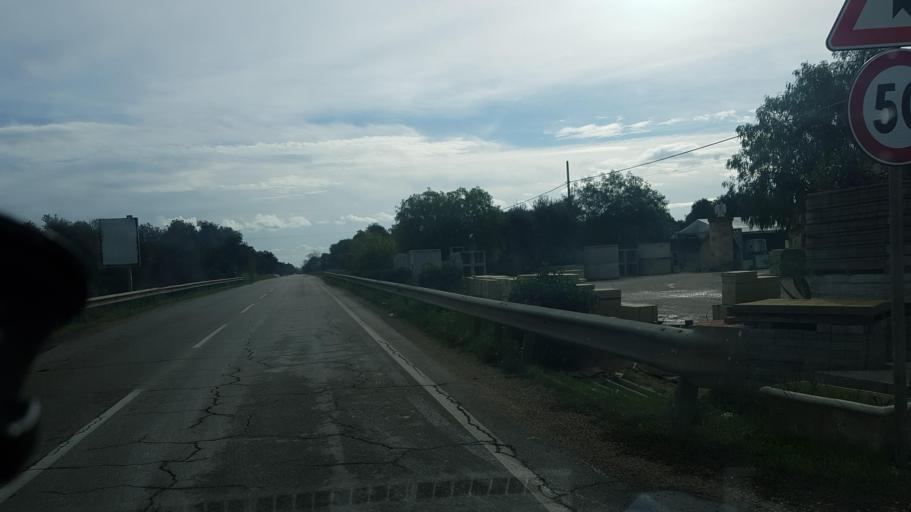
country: IT
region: Apulia
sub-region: Provincia di Brindisi
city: San Vito dei Normanni
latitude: 40.6770
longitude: 17.6875
